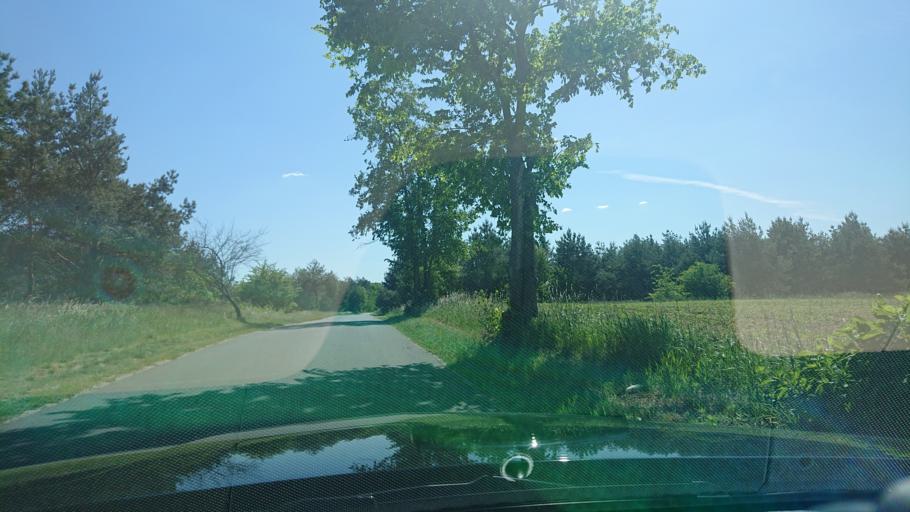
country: PL
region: Greater Poland Voivodeship
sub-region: Powiat gnieznienski
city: Gniezno
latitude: 52.4991
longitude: 17.5829
